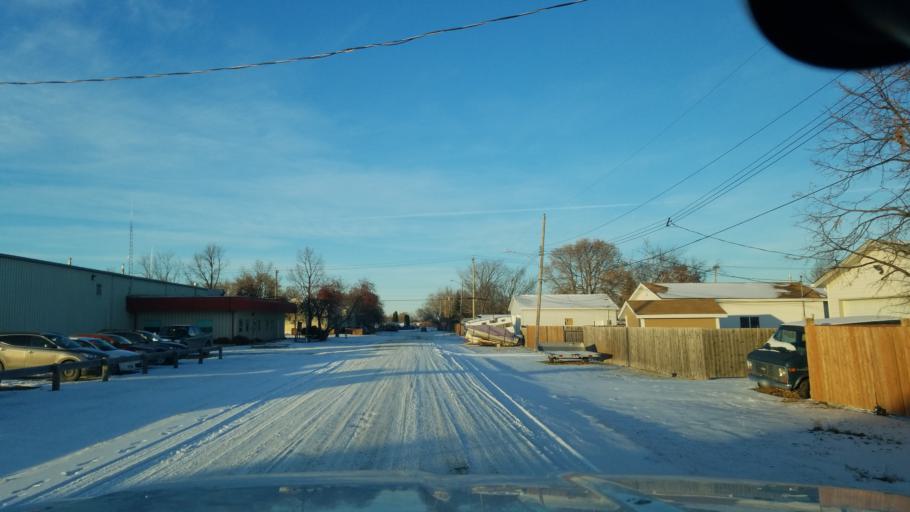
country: CA
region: Manitoba
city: Portage la Prairie
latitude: 49.9804
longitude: -98.3039
